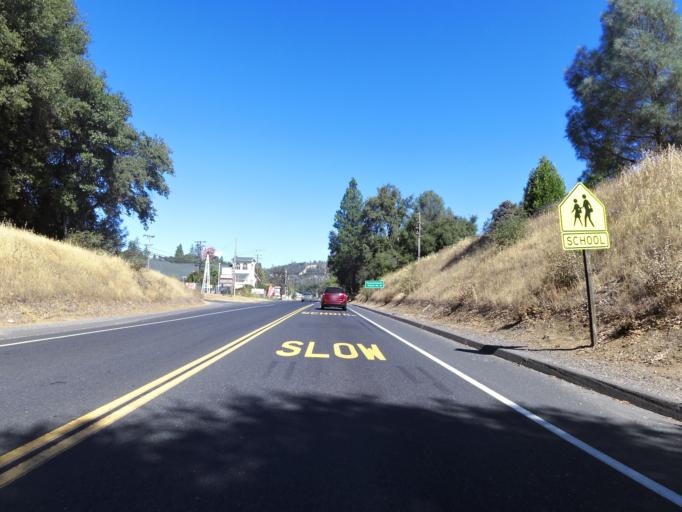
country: US
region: California
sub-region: Calaveras County
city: Murphys
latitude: 38.1325
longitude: -120.4549
